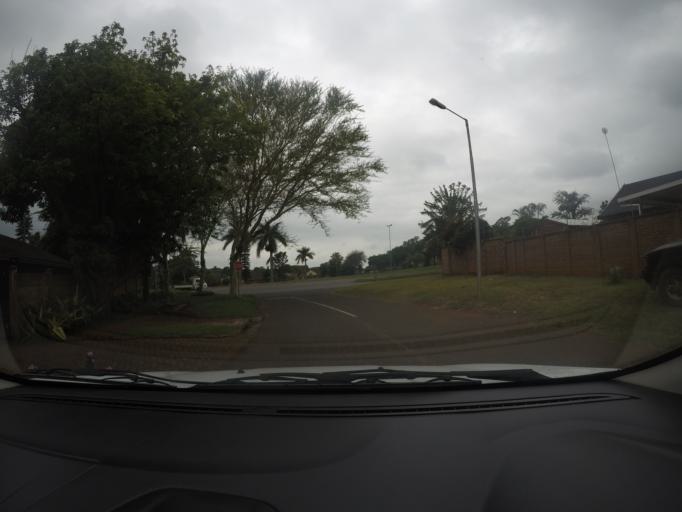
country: ZA
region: KwaZulu-Natal
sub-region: uThungulu District Municipality
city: Empangeni
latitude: -28.7603
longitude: 31.8967
